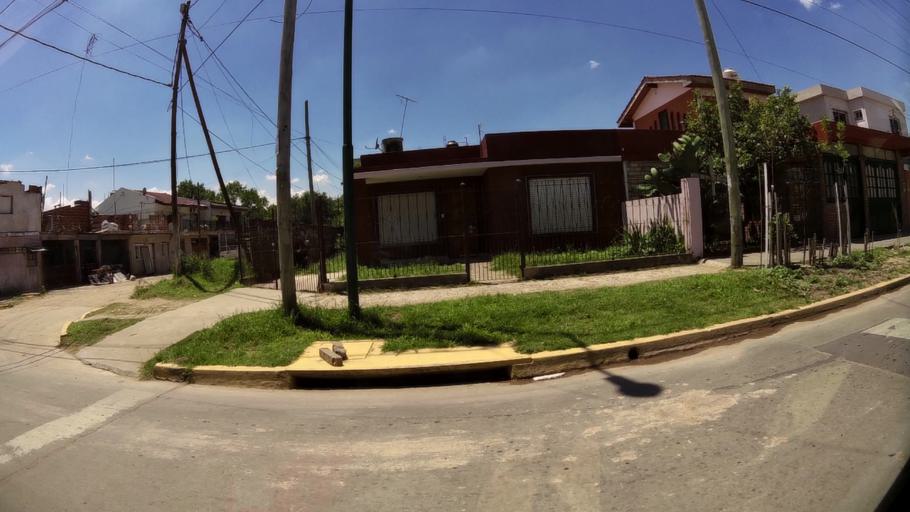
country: AR
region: Buenos Aires
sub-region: Partido de Merlo
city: Merlo
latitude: -34.6452
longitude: -58.7251
